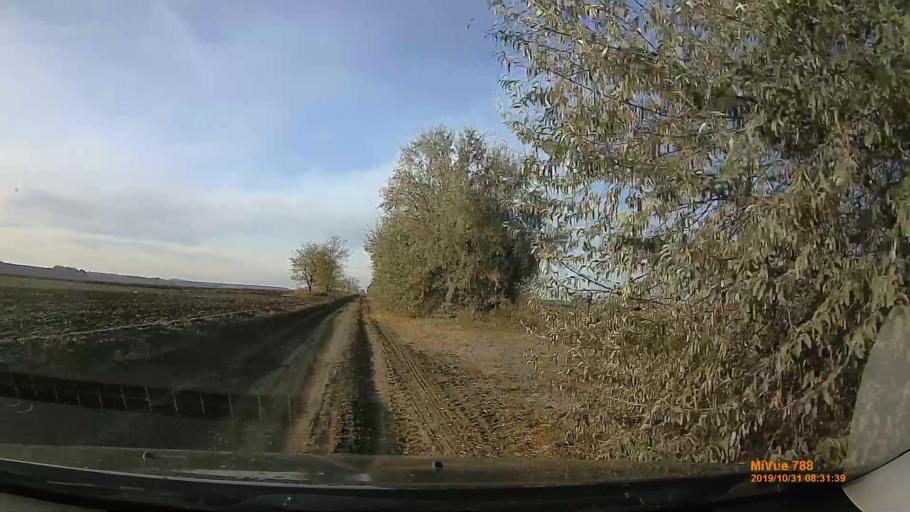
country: HU
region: Pest
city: Tapiobicske
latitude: 47.3465
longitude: 19.6653
